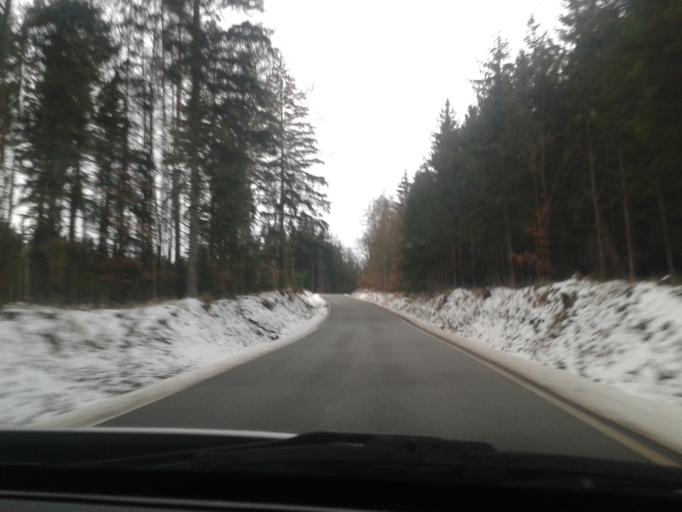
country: CZ
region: Olomoucky
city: Pteni
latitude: 49.5104
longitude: 16.9196
